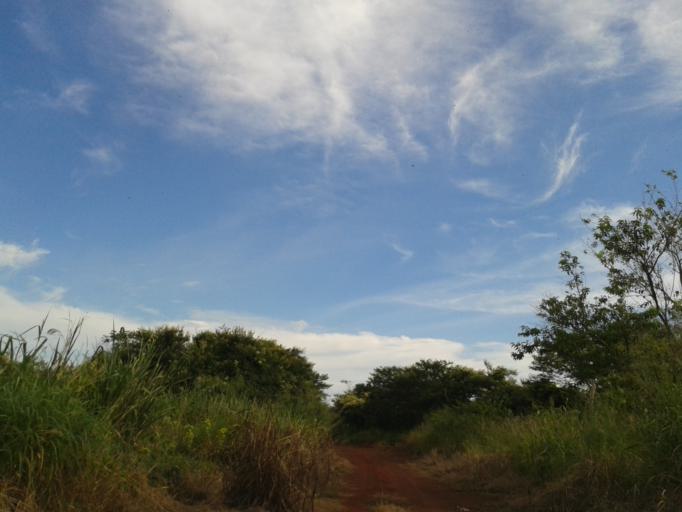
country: BR
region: Minas Gerais
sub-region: Capinopolis
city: Capinopolis
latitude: -18.6519
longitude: -49.6971
